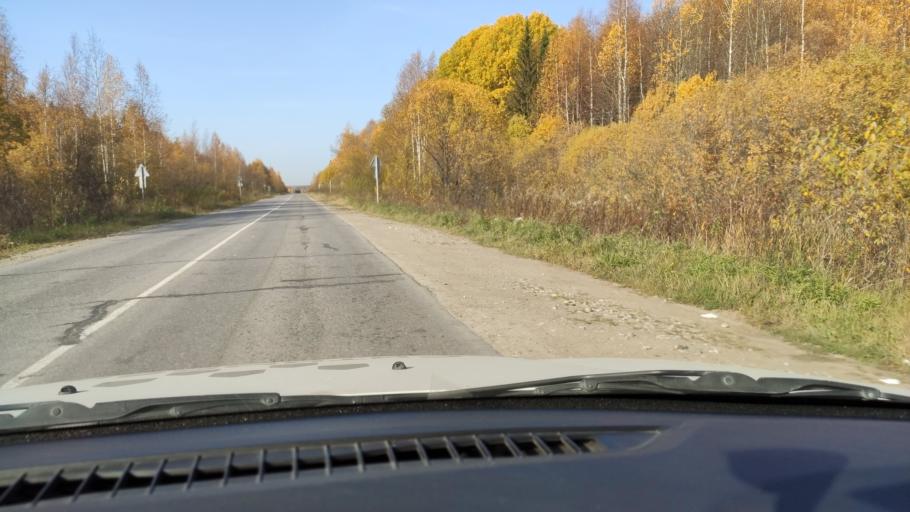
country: RU
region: Perm
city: Novyye Lyady
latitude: 58.0294
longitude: 56.6223
